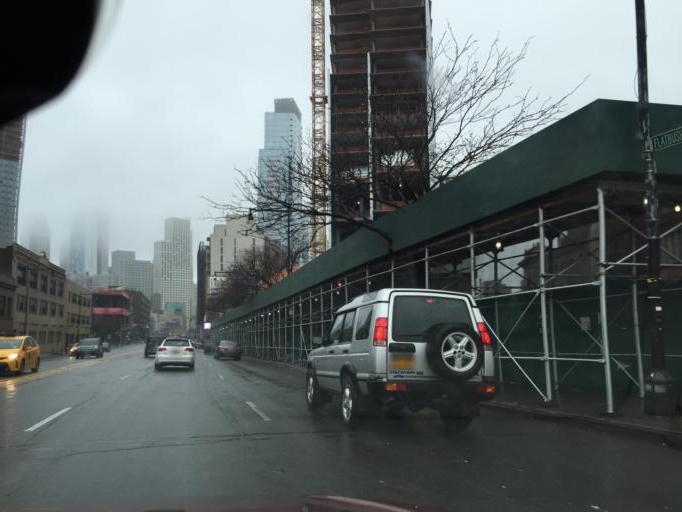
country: US
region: New York
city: New York City
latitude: 40.6852
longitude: -73.9782
